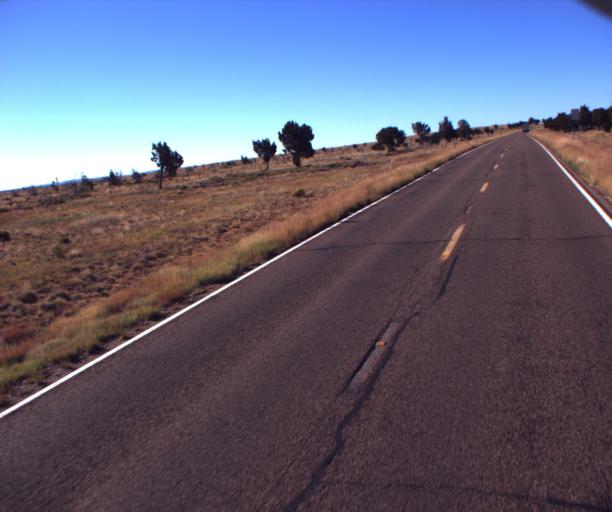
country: US
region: Arizona
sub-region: Navajo County
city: Heber-Overgaard
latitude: 34.4757
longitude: -110.4675
